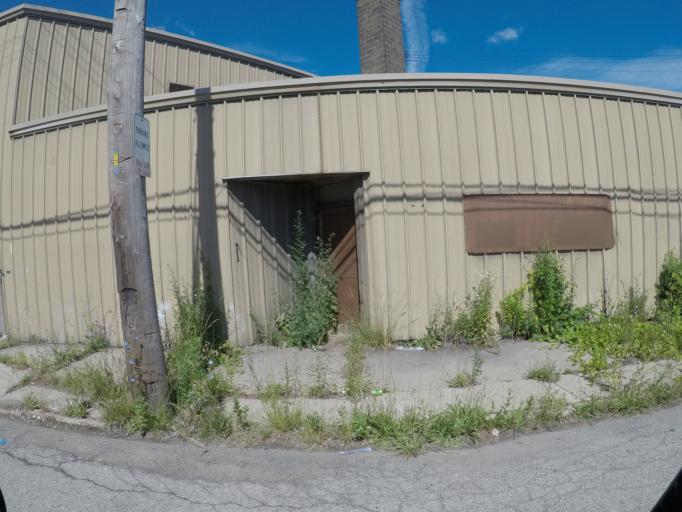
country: US
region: Michigan
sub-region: Wayne County
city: Detroit
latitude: 42.3136
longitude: -83.0811
